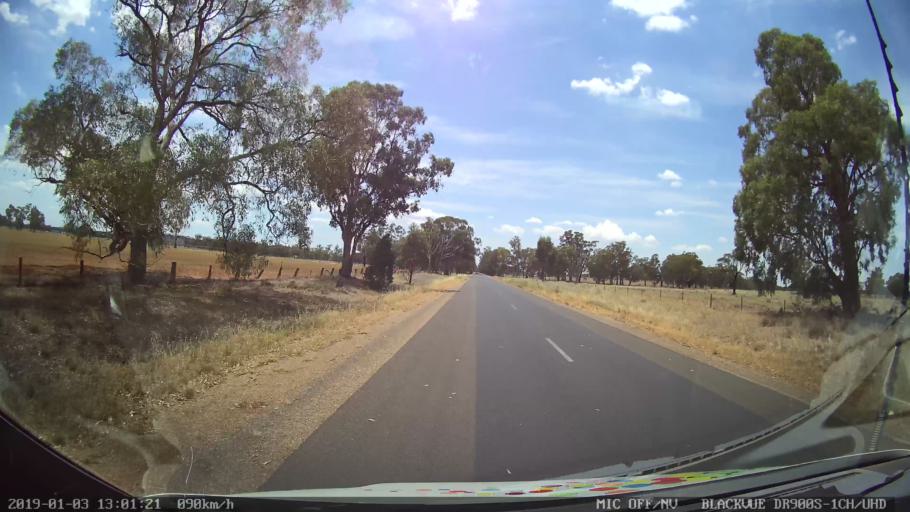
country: AU
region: New South Wales
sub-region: Cabonne
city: Canowindra
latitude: -33.6250
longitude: 148.4169
